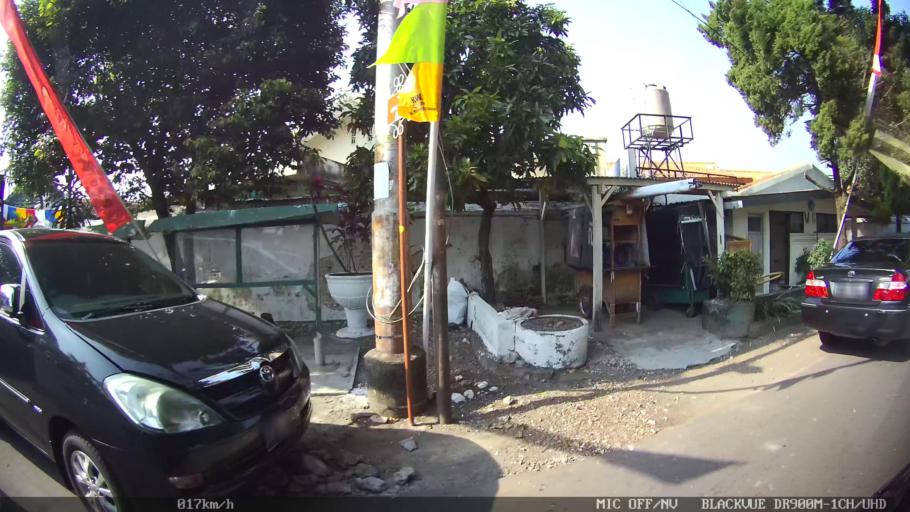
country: ID
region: Daerah Istimewa Yogyakarta
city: Yogyakarta
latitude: -7.8085
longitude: 110.3615
